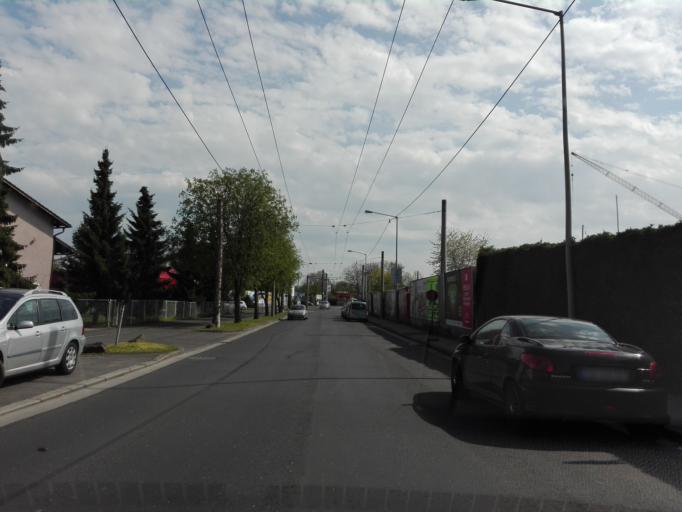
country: AT
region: Upper Austria
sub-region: Politischer Bezirk Linz-Land
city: Ansfelden
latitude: 48.2475
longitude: 14.2858
